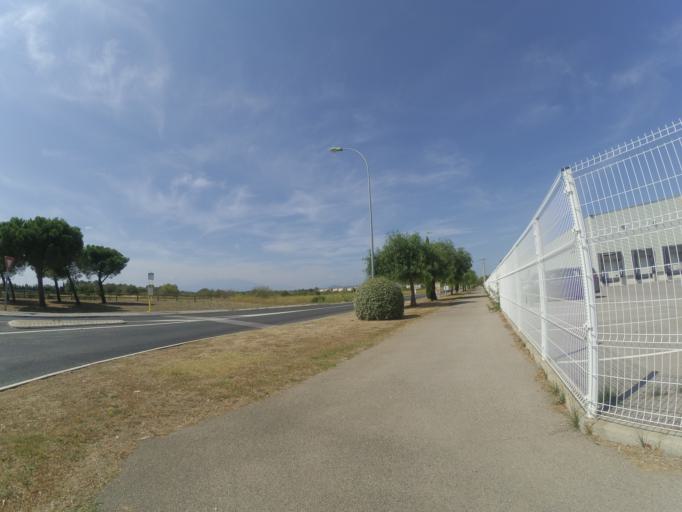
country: FR
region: Languedoc-Roussillon
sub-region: Departement des Pyrenees-Orientales
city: Rivesaltes
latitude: 42.7795
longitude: 2.8823
